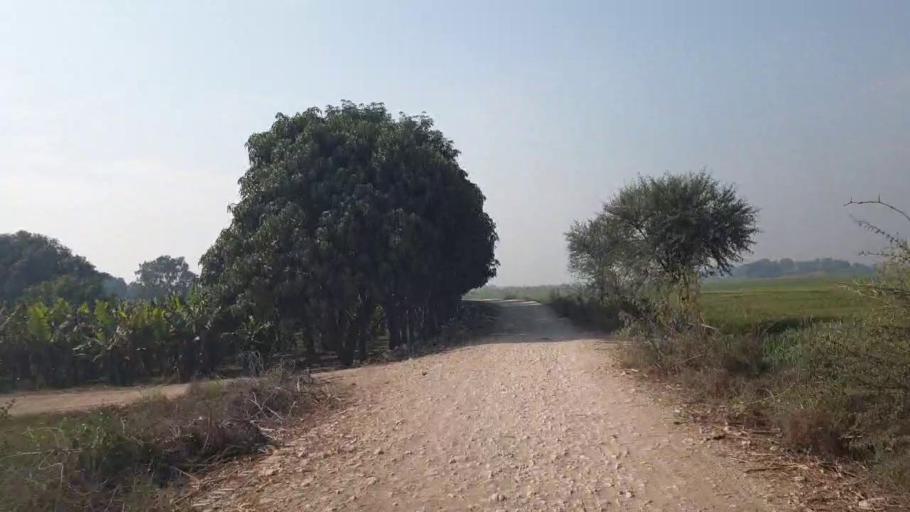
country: PK
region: Sindh
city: Tando Allahyar
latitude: 25.3846
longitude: 68.7695
